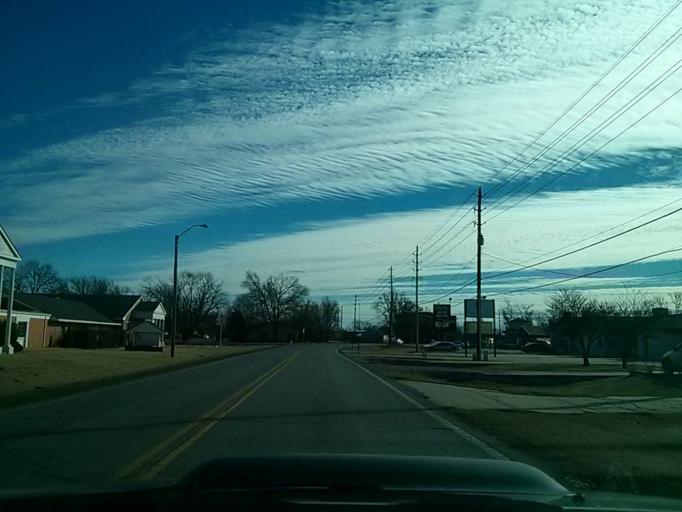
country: US
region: Oklahoma
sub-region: Tulsa County
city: Jenks
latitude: 36.0242
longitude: -95.9832
